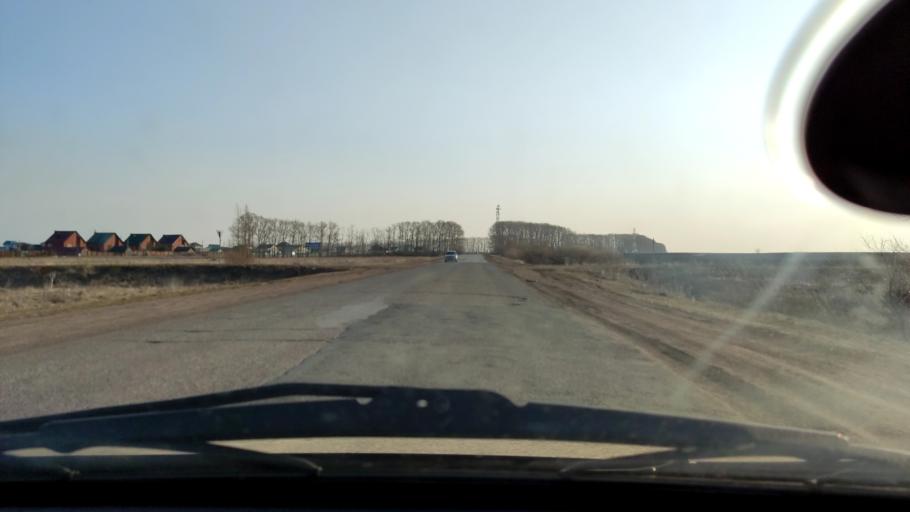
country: RU
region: Bashkortostan
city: Asanovo
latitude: 54.8126
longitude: 55.5810
